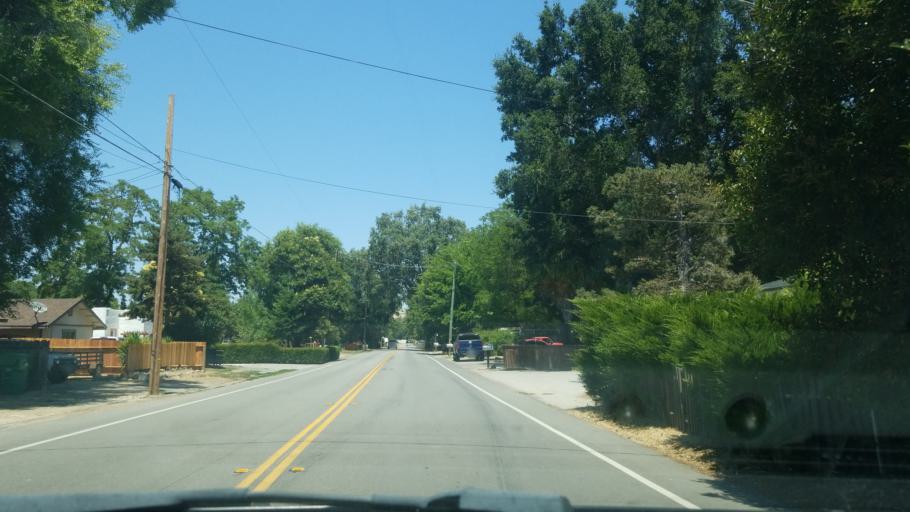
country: US
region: California
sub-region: San Luis Obispo County
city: Atascadero
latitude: 35.4959
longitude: -120.6640
